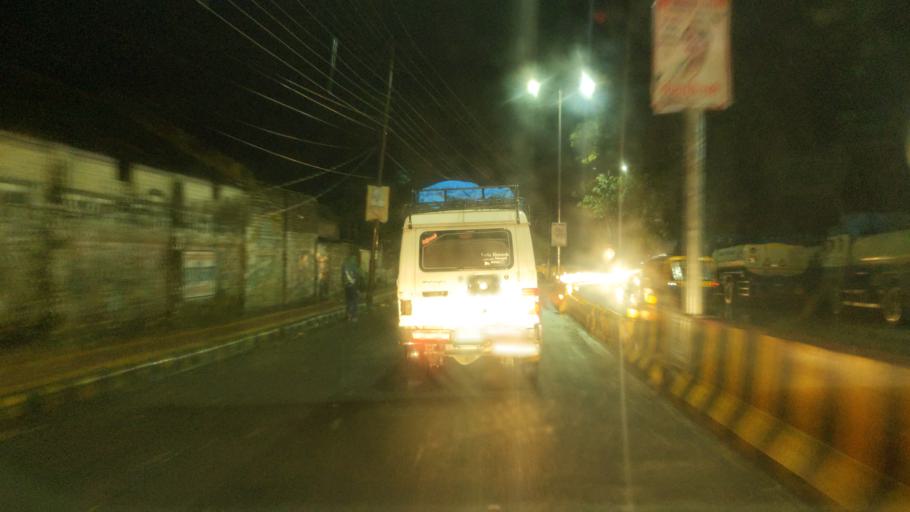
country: IN
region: Uttarakhand
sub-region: Naini Tal
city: Haldwani
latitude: 29.2642
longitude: 79.5445
